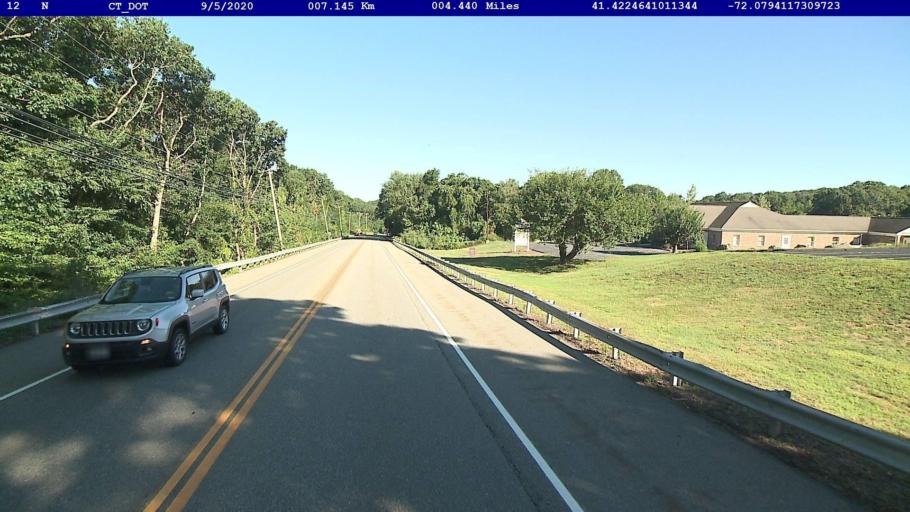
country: US
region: Connecticut
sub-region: New London County
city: Gales Ferry
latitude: 41.4225
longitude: -72.0794
